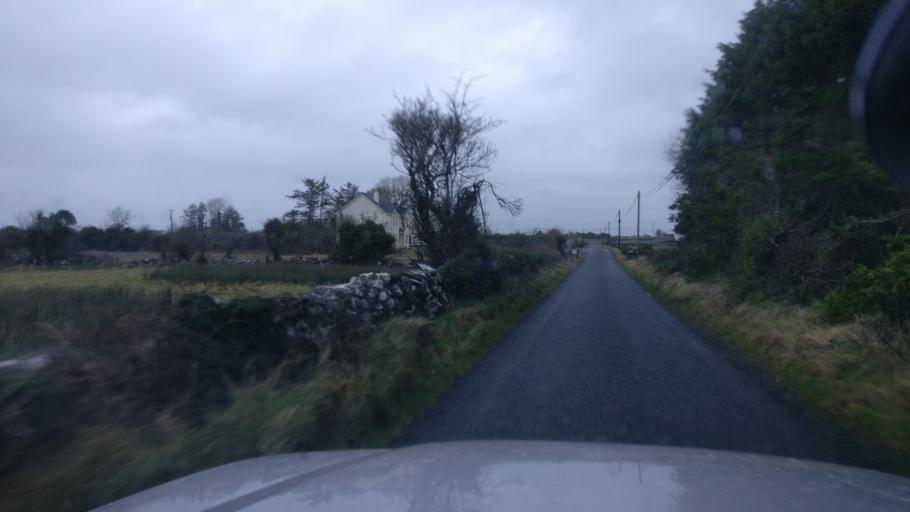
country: IE
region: Connaught
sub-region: County Galway
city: Loughrea
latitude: 53.2162
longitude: -8.6242
